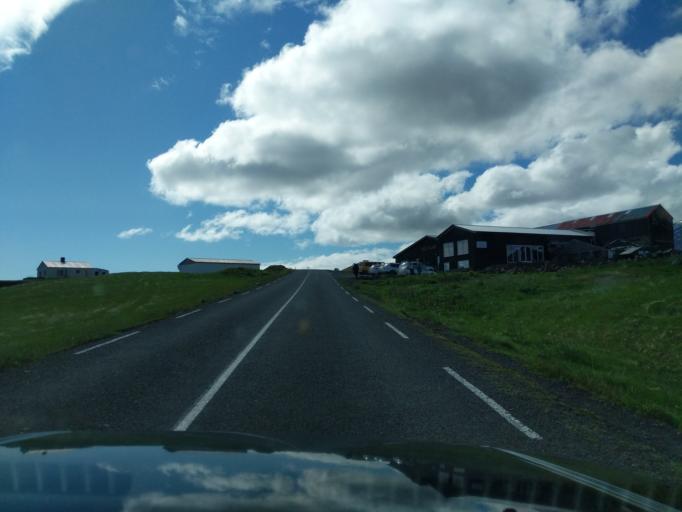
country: IS
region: West
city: Olafsvik
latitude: 64.7505
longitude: -23.6508
